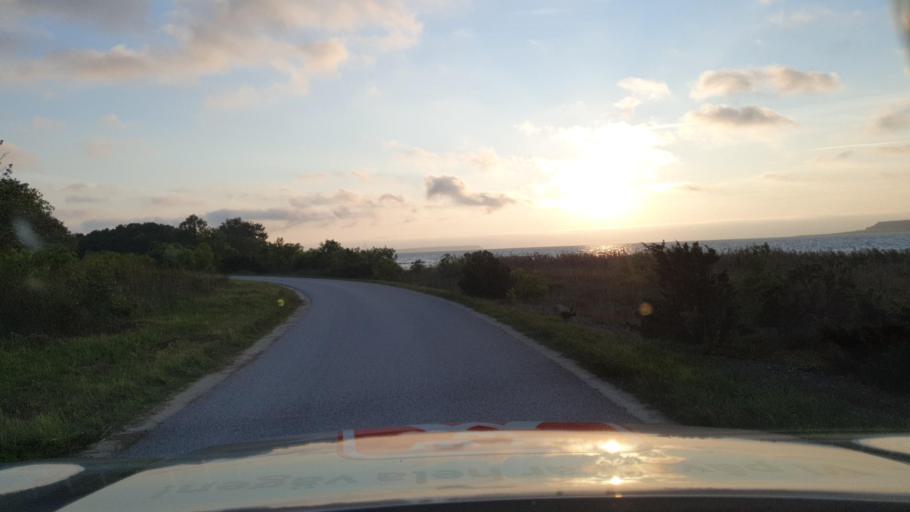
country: SE
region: Gotland
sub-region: Gotland
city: Klintehamn
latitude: 57.2932
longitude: 18.1156
